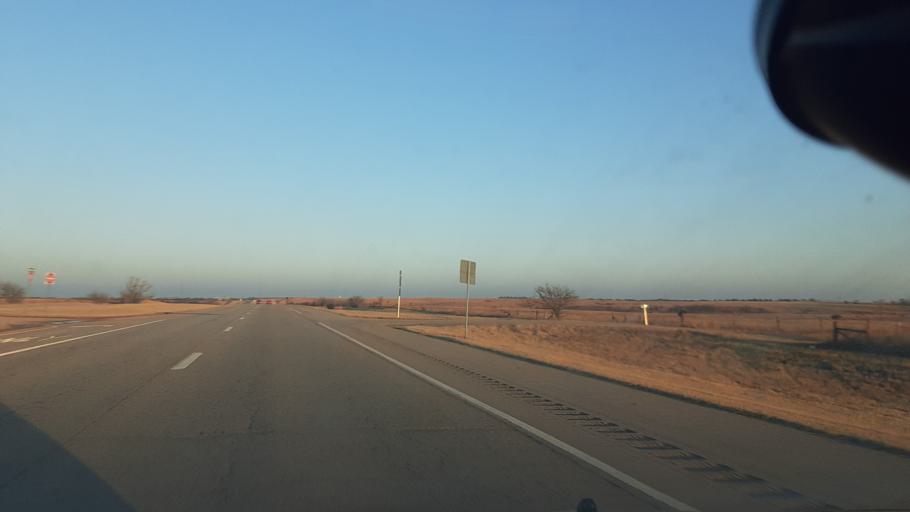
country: US
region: Oklahoma
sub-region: Noble County
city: Perry
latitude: 36.3980
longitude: -97.3730
